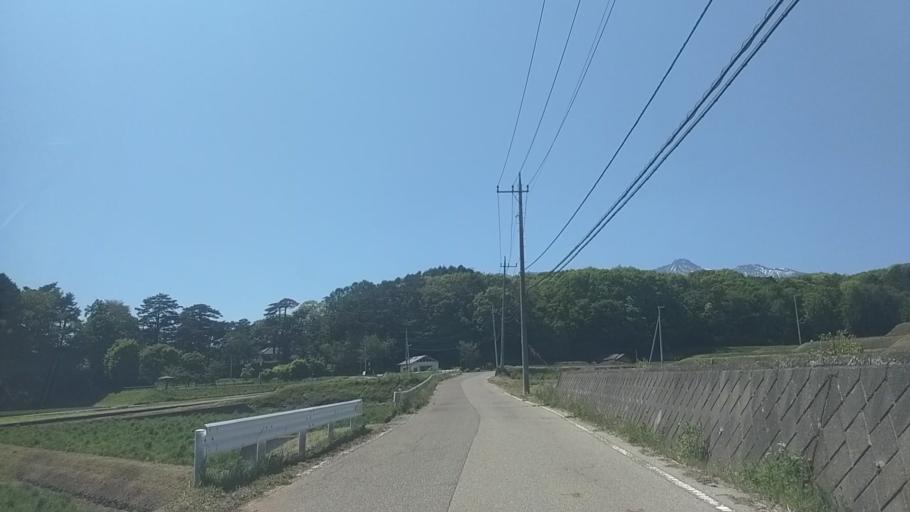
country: JP
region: Yamanashi
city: Nirasaki
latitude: 35.8896
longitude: 138.4570
